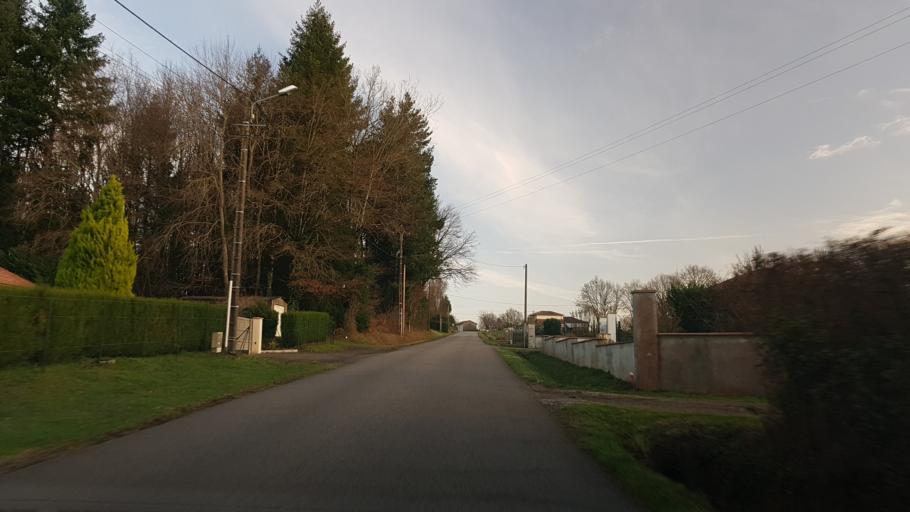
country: FR
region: Limousin
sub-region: Departement de la Haute-Vienne
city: Saint-Junien
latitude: 45.8974
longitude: 0.8646
